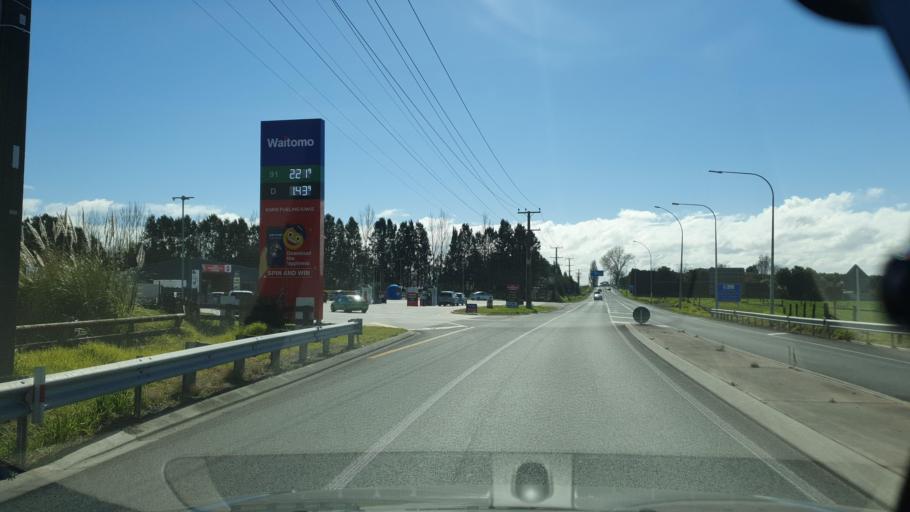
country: NZ
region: Bay of Plenty
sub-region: Tauranga City
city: Tauranga
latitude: -37.7220
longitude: 176.2844
